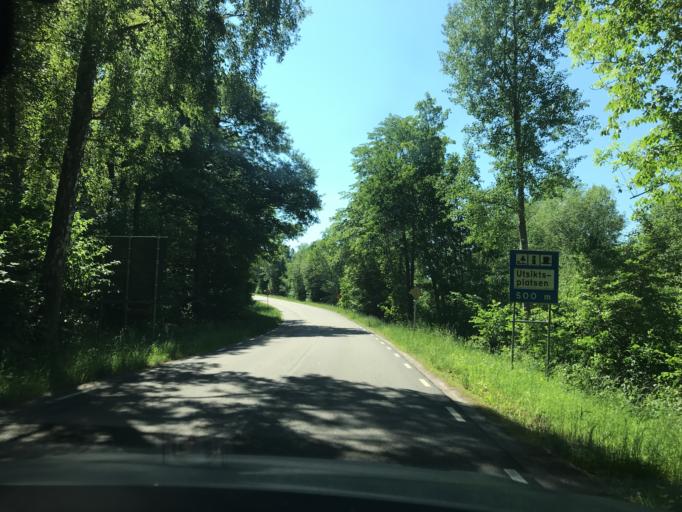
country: SE
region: Vaestra Goetaland
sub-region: Gotene Kommun
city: Goetene
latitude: 58.6223
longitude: 13.4082
